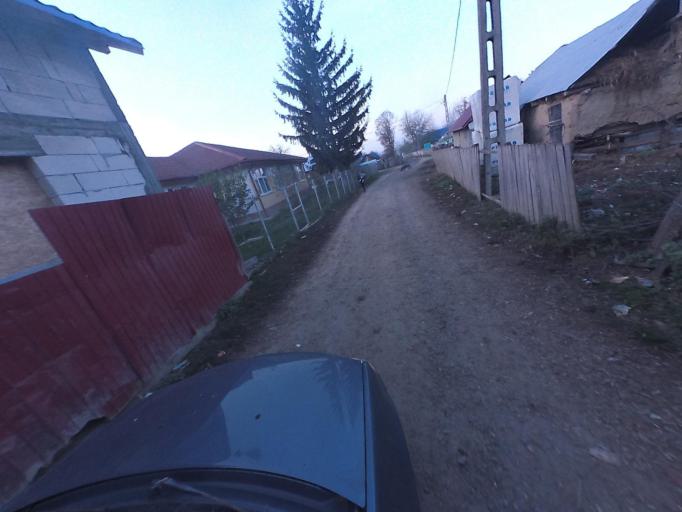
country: RO
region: Vaslui
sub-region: Comuna Garceni
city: Garceni
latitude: 46.7882
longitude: 27.2438
